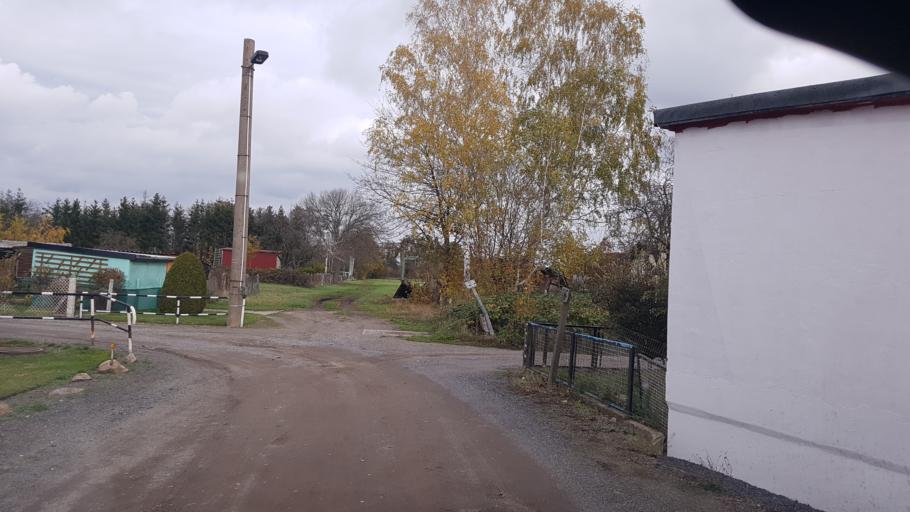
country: DE
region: Brandenburg
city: Doberlug-Kirchhain
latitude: 51.6415
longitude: 13.5728
